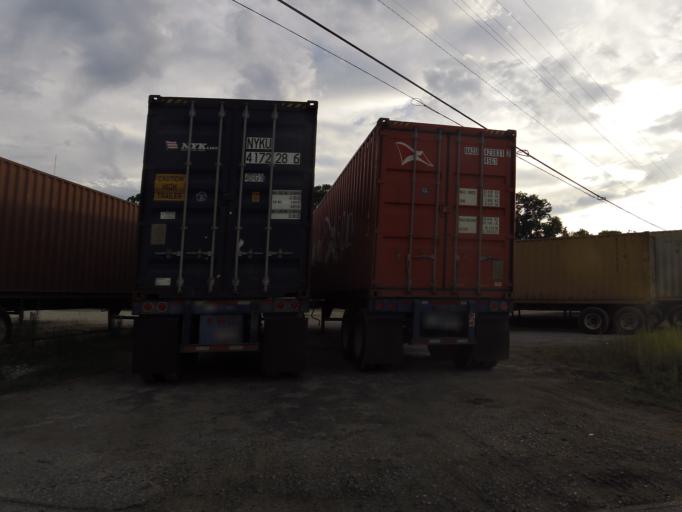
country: US
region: Georgia
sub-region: Chatham County
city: Pooler
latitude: 32.0935
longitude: -81.2010
